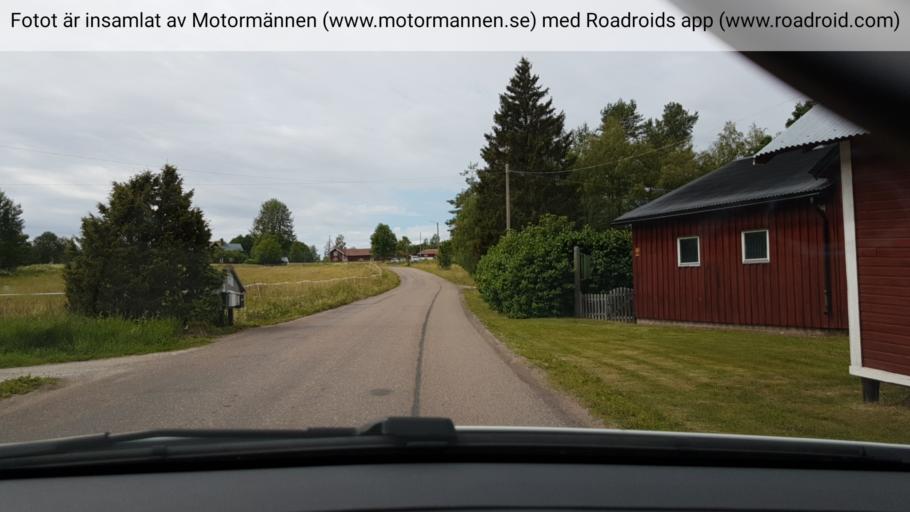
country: SE
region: Dalarna
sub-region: Rattviks Kommun
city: Raettvik
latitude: 60.9286
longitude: 15.1233
